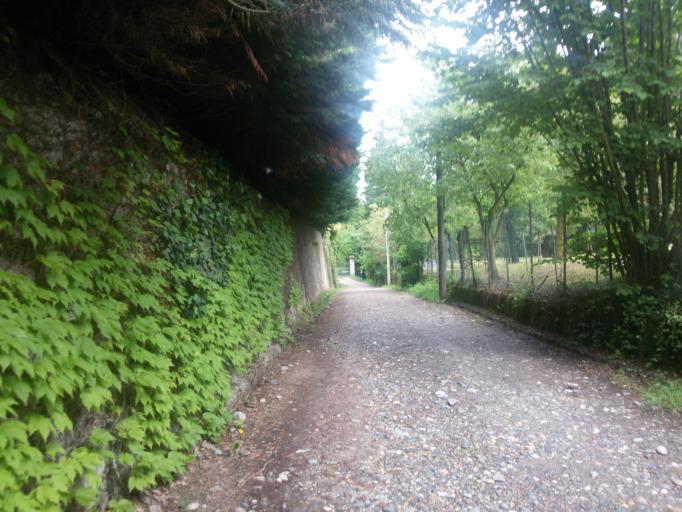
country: IT
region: Piedmont
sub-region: Provincia di Torino
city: Turin
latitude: 45.0452
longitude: 7.6937
